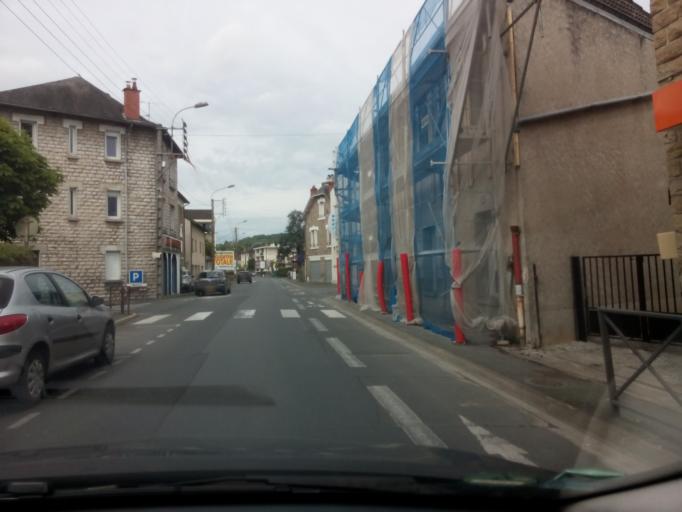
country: FR
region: Limousin
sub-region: Departement de la Correze
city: Brive-la-Gaillarde
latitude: 45.1658
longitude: 1.5278
